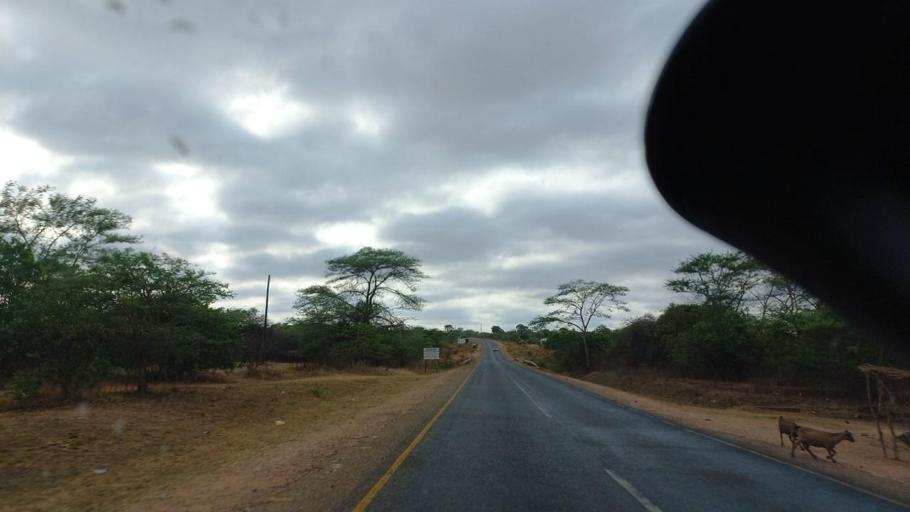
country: ZM
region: Lusaka
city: Chongwe
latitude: -15.2906
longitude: 28.8008
